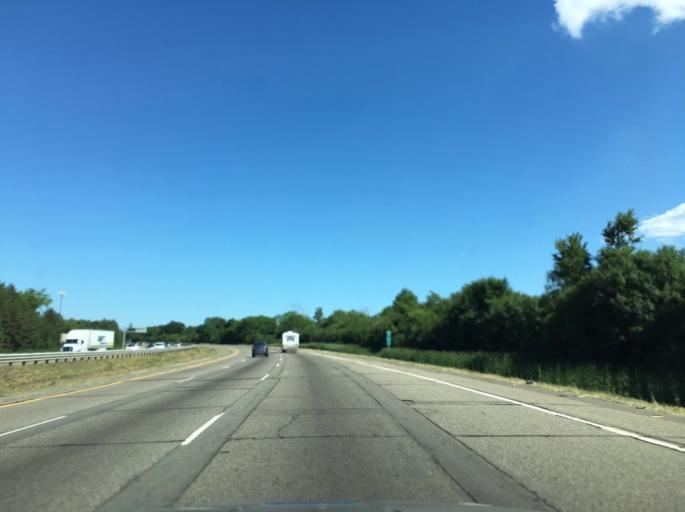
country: US
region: Michigan
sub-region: Oakland County
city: Troy
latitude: 42.6007
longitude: -83.1633
